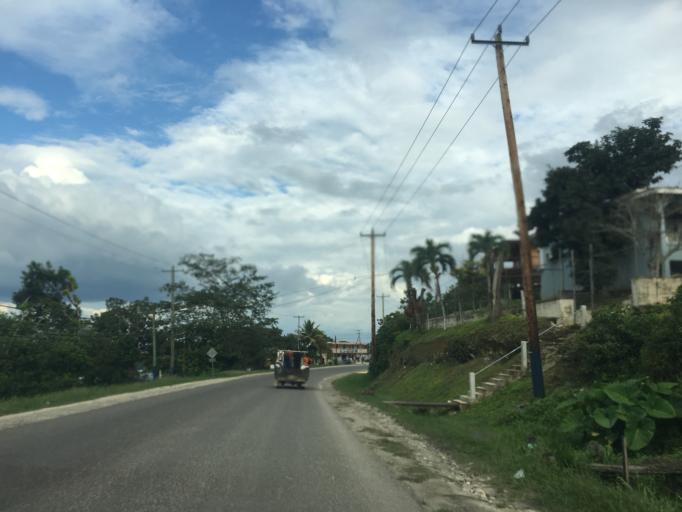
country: BZ
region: Cayo
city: San Ignacio
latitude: 17.1482
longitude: -89.0792
